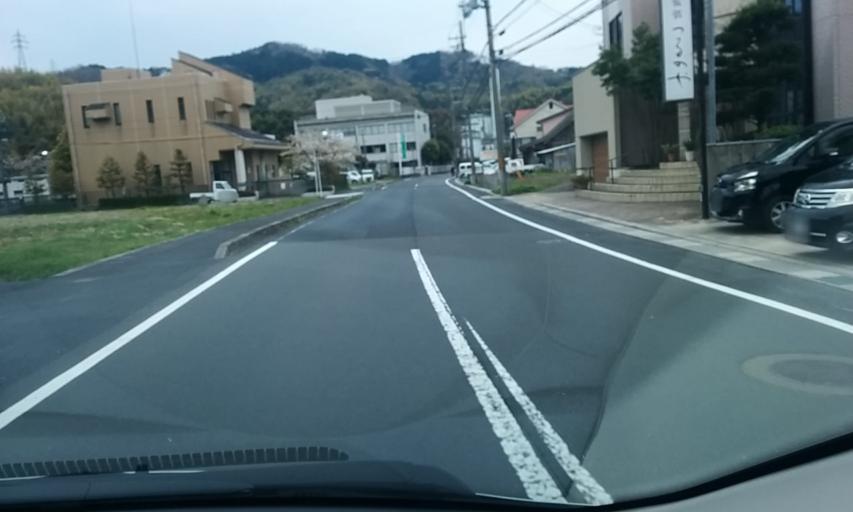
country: JP
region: Kyoto
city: Miyazu
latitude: 35.5527
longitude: 135.2101
